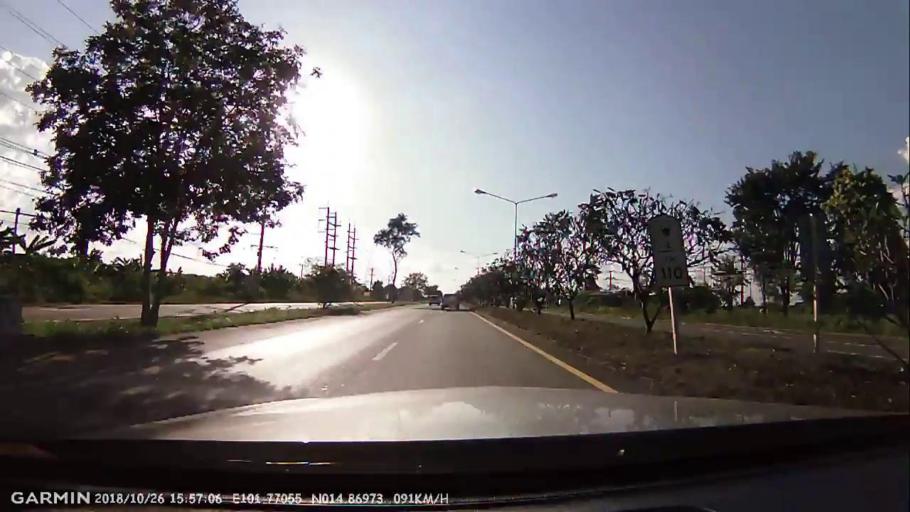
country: TH
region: Nakhon Ratchasima
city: Sikhio
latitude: 14.8697
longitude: 101.7704
